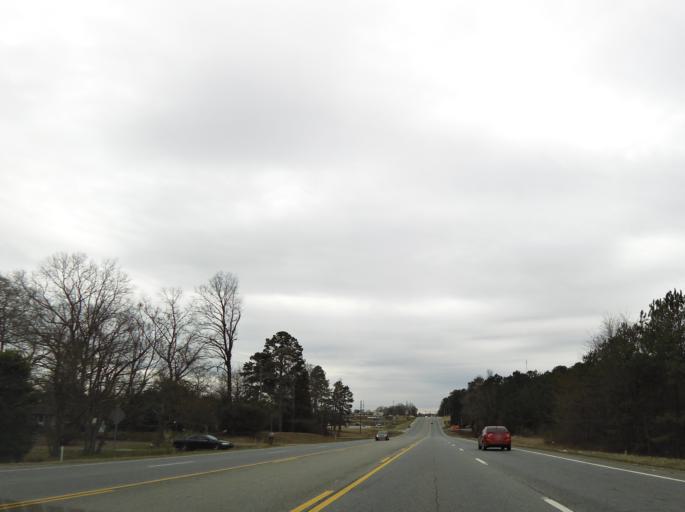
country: US
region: Georgia
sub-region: Houston County
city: Robins Air Force Base
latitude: 32.5730
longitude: -83.5918
